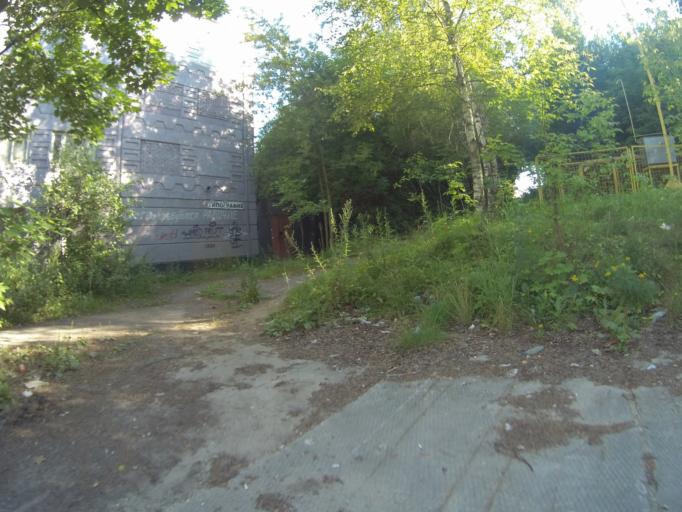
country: RU
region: Vladimir
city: Vladimir
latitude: 56.1626
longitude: 40.3823
